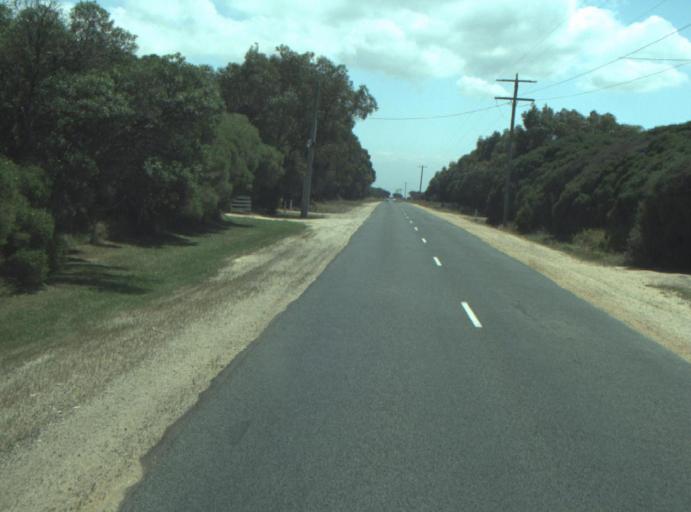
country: AU
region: Victoria
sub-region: Greater Geelong
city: Breakwater
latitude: -38.2754
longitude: 144.4025
